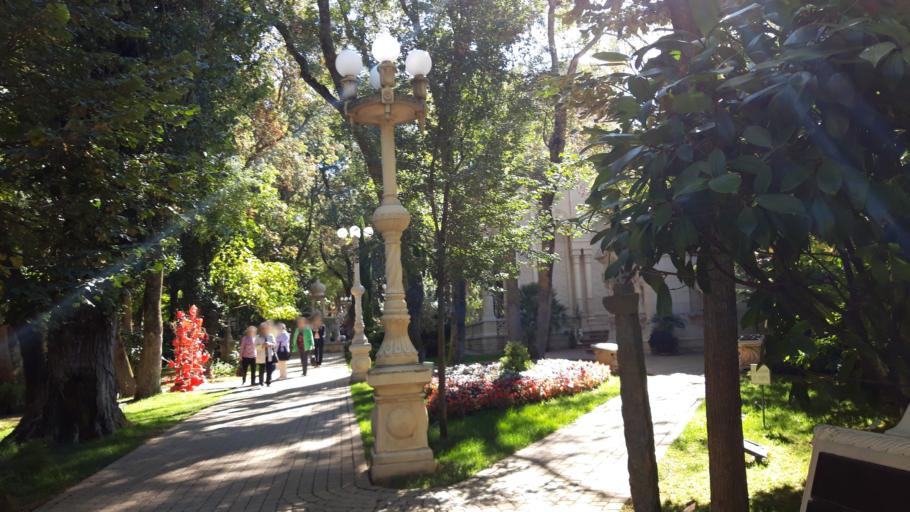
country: RU
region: Krasnodarskiy
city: Kabardinka
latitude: 44.6450
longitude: 37.9347
